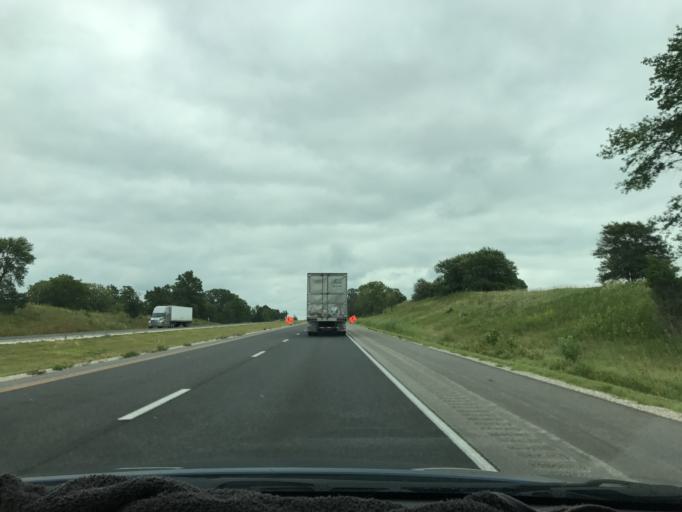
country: US
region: Illinois
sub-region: Henry County
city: Geneseo
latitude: 41.4142
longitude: -90.0762
